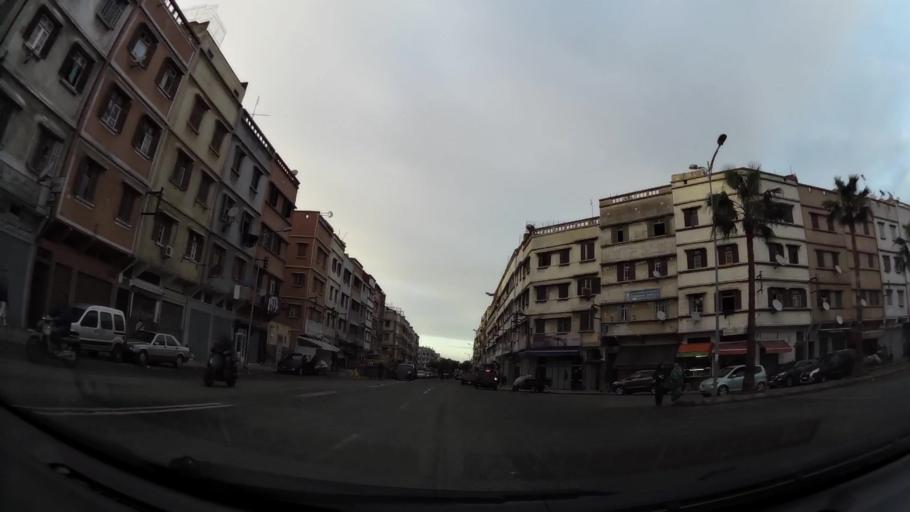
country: MA
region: Grand Casablanca
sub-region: Casablanca
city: Casablanca
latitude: 33.5599
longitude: -7.6008
